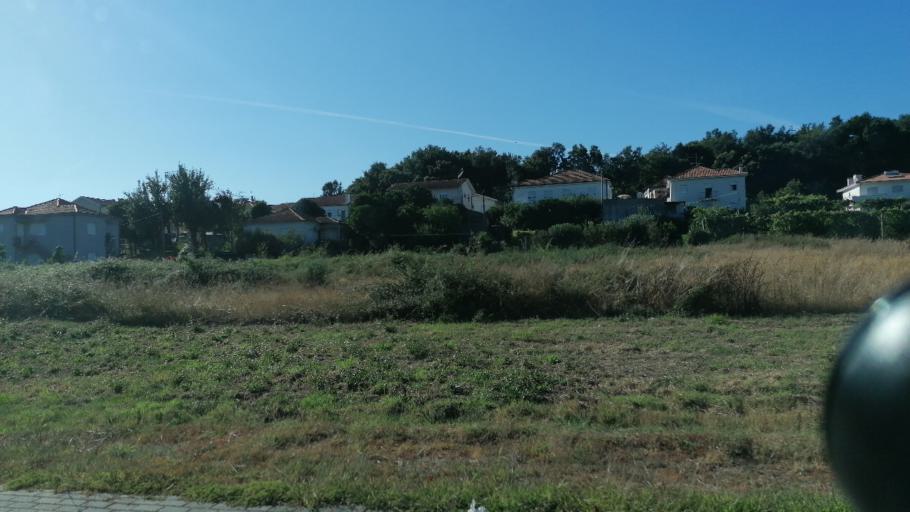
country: PT
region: Porto
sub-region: Santo Tirso
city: Santo Tirso
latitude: 41.3544
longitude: -8.4668
